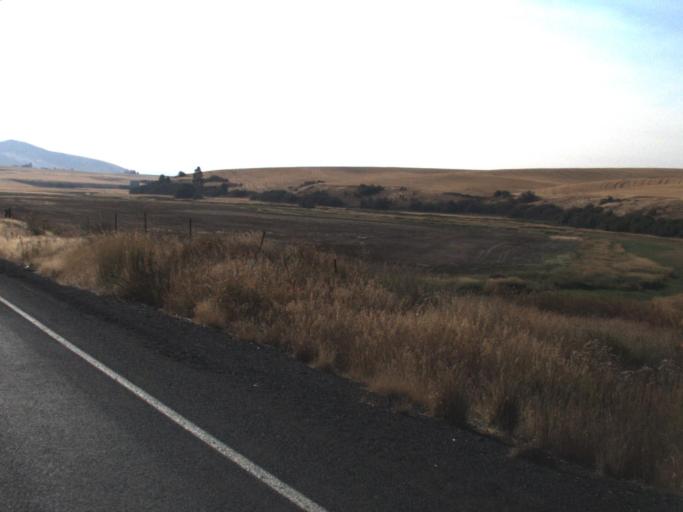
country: US
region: Idaho
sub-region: Benewah County
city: Plummer
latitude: 47.3254
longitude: -117.1856
